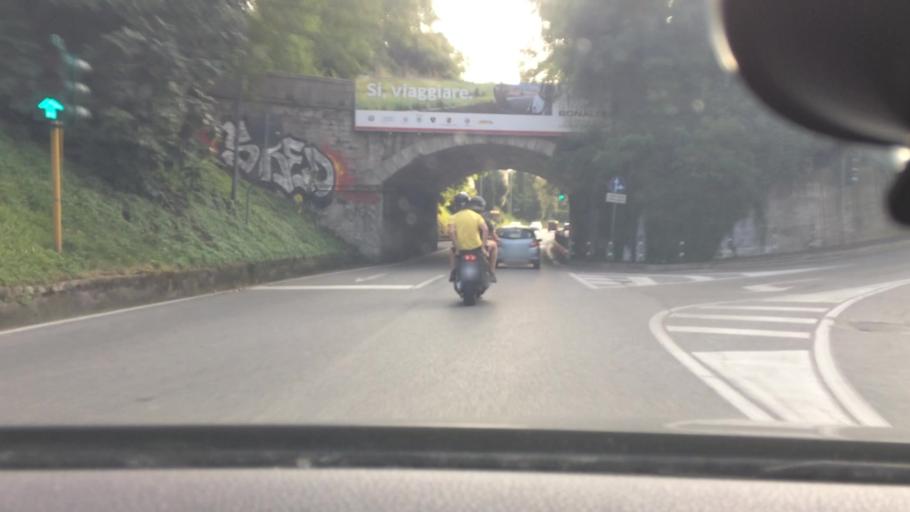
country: IT
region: Lombardy
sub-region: Provincia di Bergamo
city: Curno
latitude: 45.6931
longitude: 9.6071
